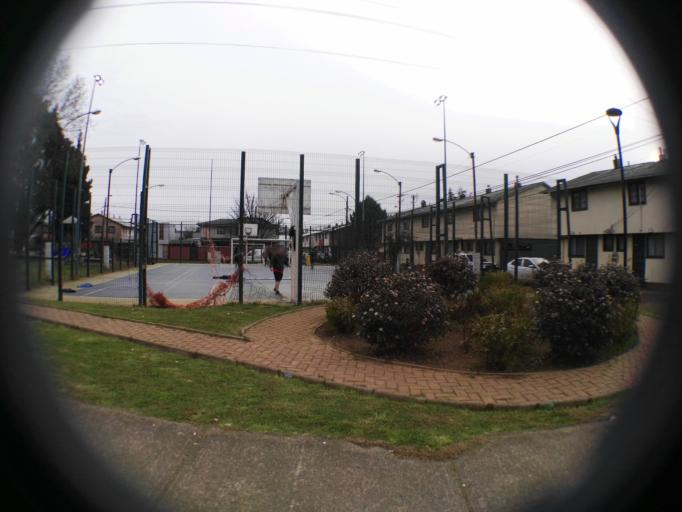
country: CL
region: Los Rios
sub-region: Provincia de Valdivia
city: Valdivia
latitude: -39.8288
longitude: -73.2352
